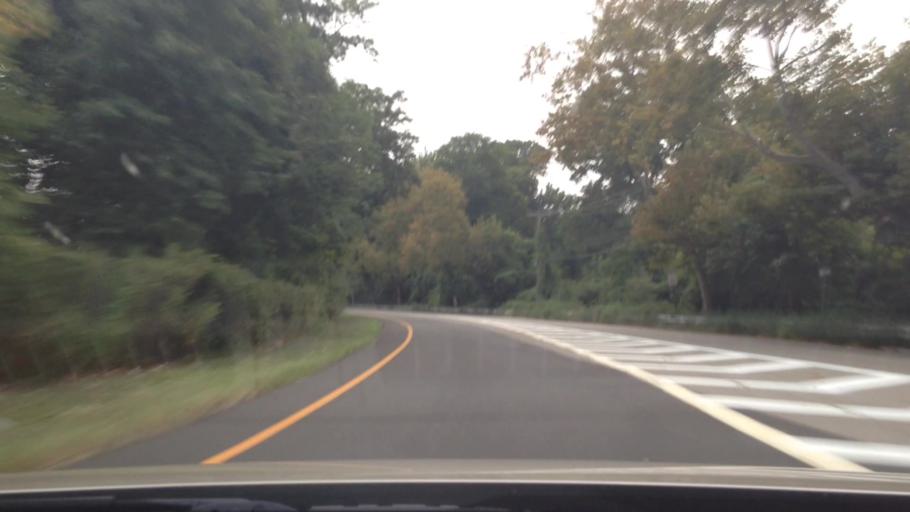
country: US
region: New York
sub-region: Nassau County
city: North Hills
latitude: 40.7728
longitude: -73.6840
